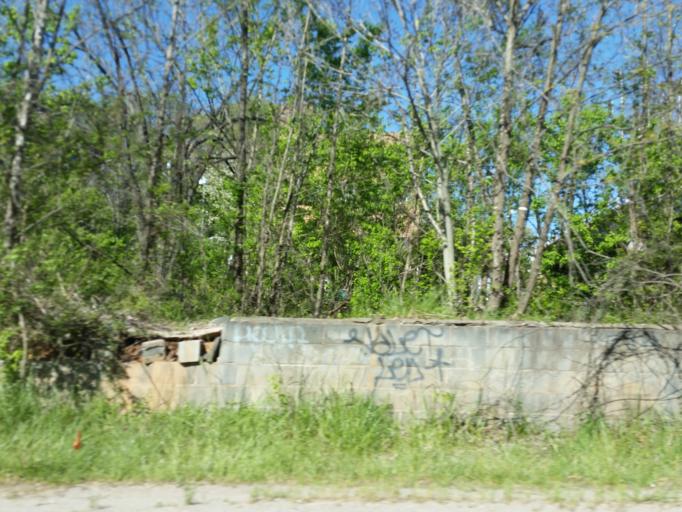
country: US
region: North Carolina
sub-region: Buncombe County
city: Asheville
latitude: 35.5865
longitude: -82.5678
